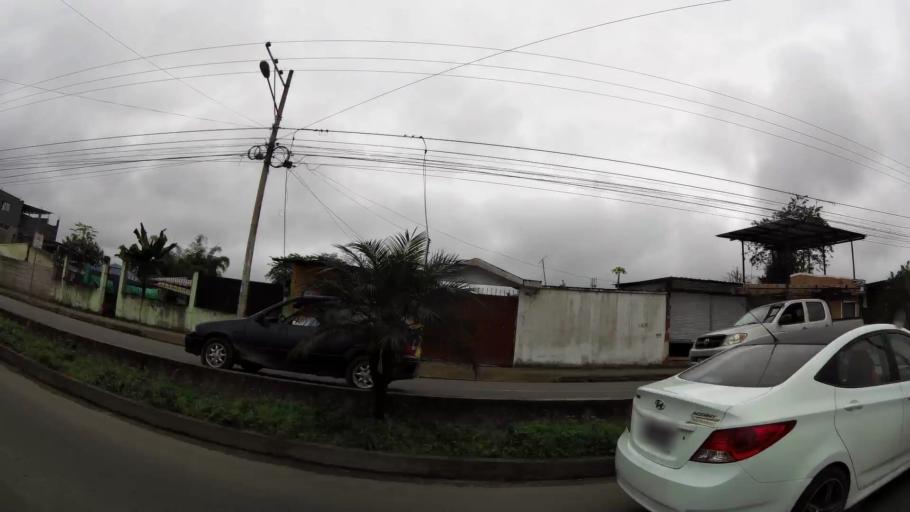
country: EC
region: Santo Domingo de los Tsachilas
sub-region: Canton Santo Domingo de los Colorados
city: Santo Domingo de los Colorados
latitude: -0.2675
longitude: -79.1985
